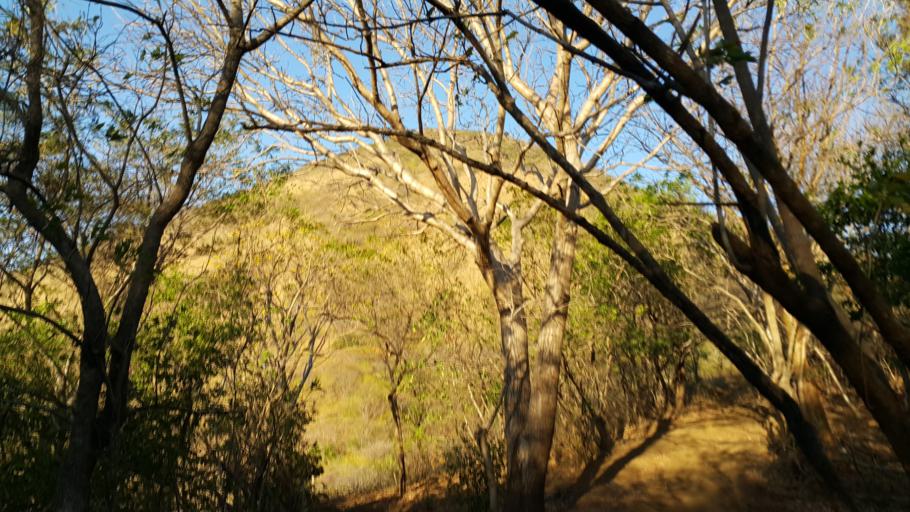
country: NI
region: Leon
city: La Paz Centro
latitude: 12.4938
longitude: -86.6937
